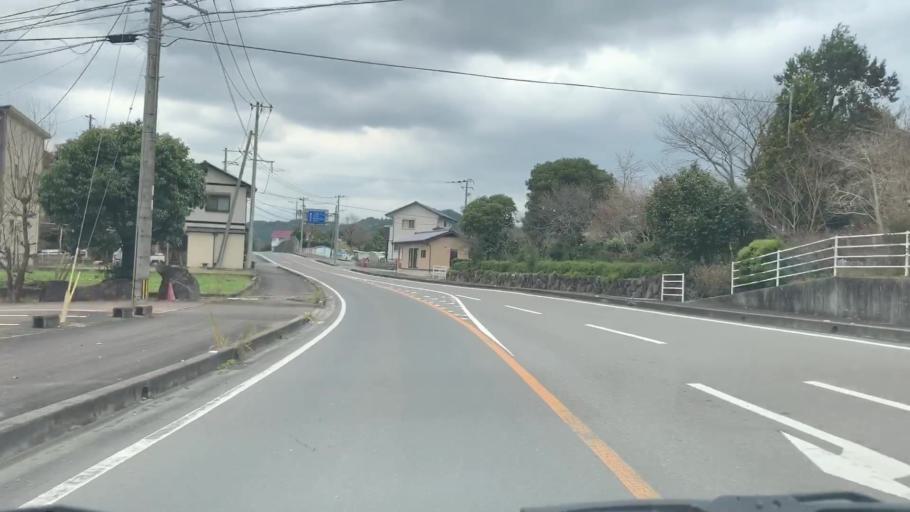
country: JP
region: Saga Prefecture
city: Ureshinomachi-shimojuku
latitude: 33.1367
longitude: 129.9878
